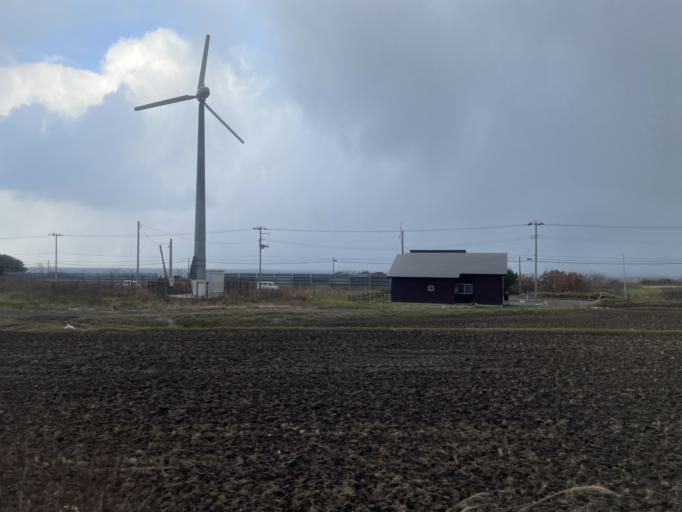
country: JP
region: Aomori
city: Mutsu
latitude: 41.1251
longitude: 141.2661
